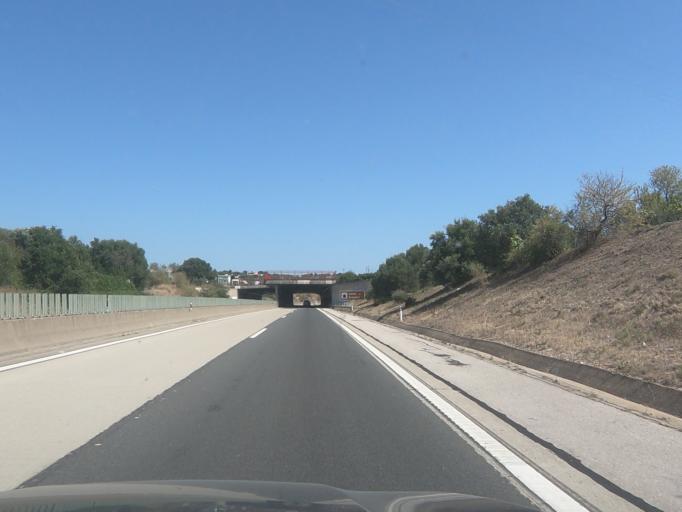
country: PT
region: Faro
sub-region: Loule
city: Loule
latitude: 37.1134
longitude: -8.0236
